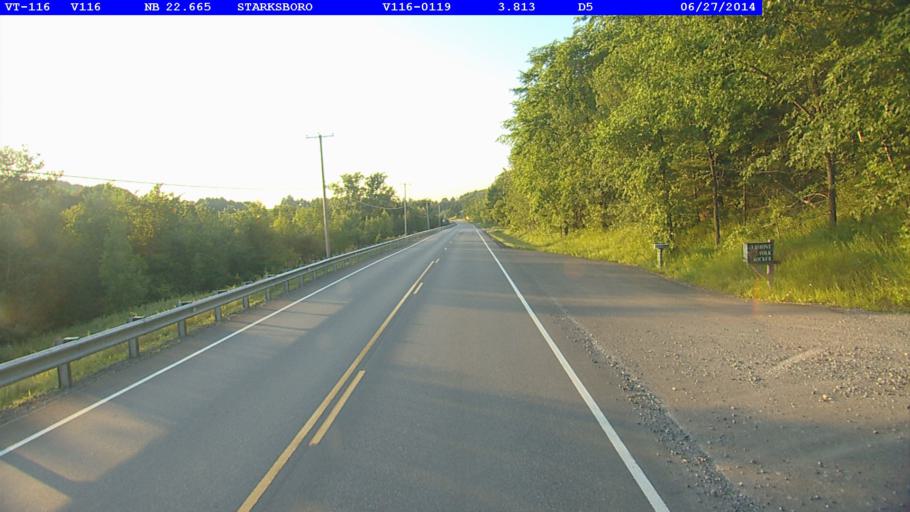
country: US
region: Vermont
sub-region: Chittenden County
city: Hinesburg
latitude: 44.2396
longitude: -73.0580
